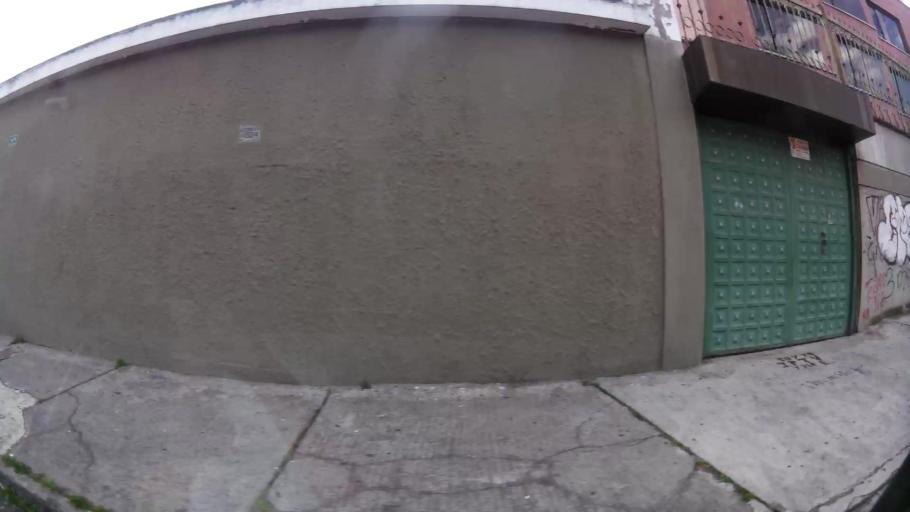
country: EC
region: Pichincha
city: Quito
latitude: -0.1318
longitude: -78.4842
